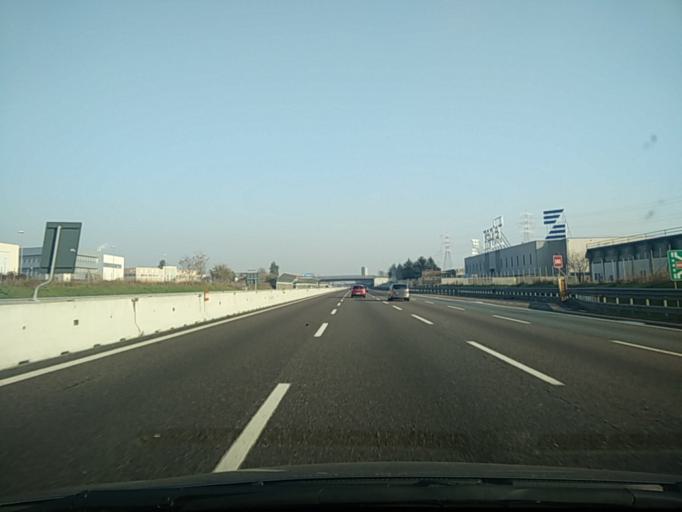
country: IT
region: Lombardy
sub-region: Provincia di Monza e Brianza
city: Brugherio
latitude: 45.5591
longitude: 9.2890
